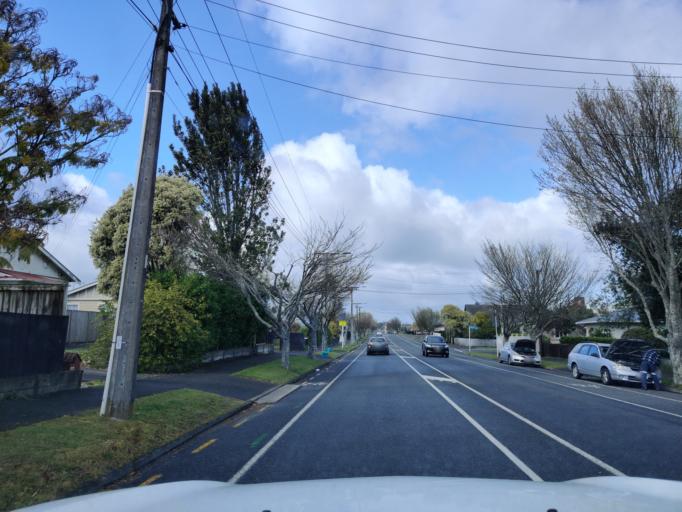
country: NZ
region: Waikato
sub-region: Hamilton City
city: Hamilton
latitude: -37.7848
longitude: 175.2519
